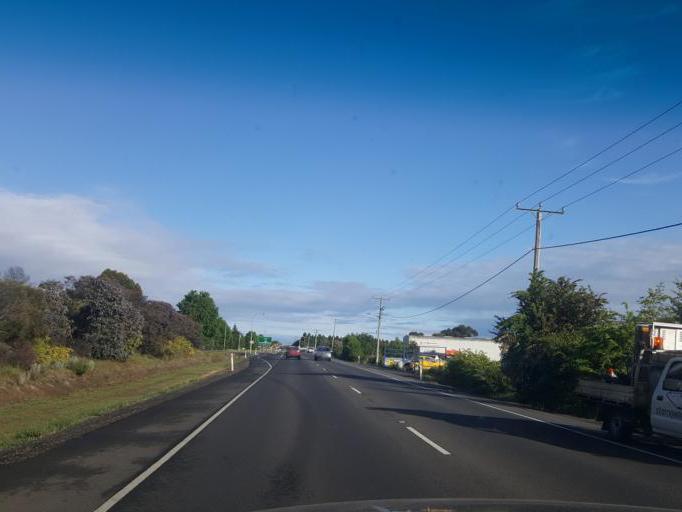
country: AU
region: Tasmania
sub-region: Northern Midlands
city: Perth
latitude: -41.5389
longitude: 147.1986
